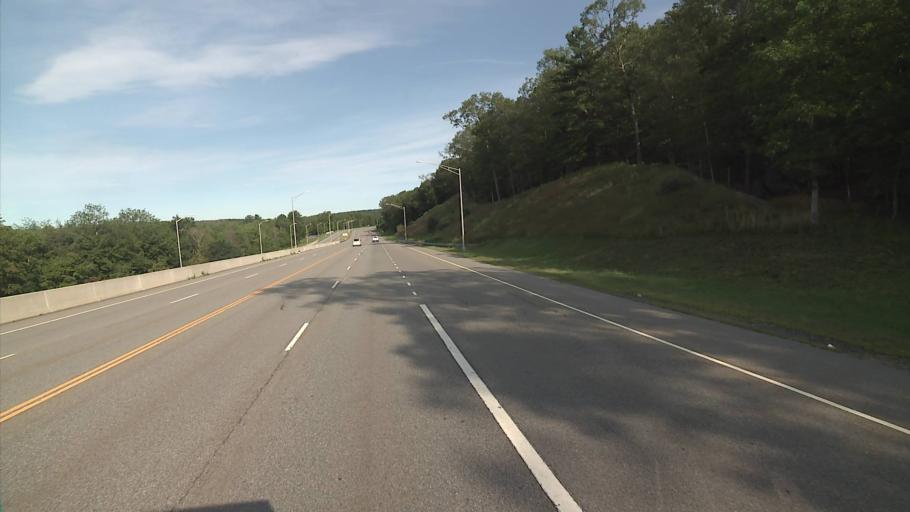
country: US
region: Connecticut
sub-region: New London County
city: Preston City
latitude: 41.4795
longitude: -71.9622
